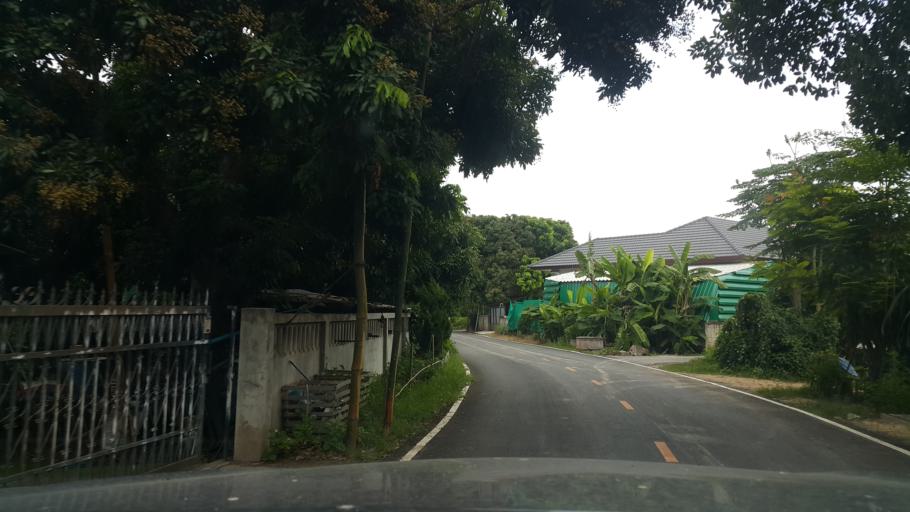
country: TH
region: Lamphun
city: Ban Thi
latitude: 18.6628
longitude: 99.1541
